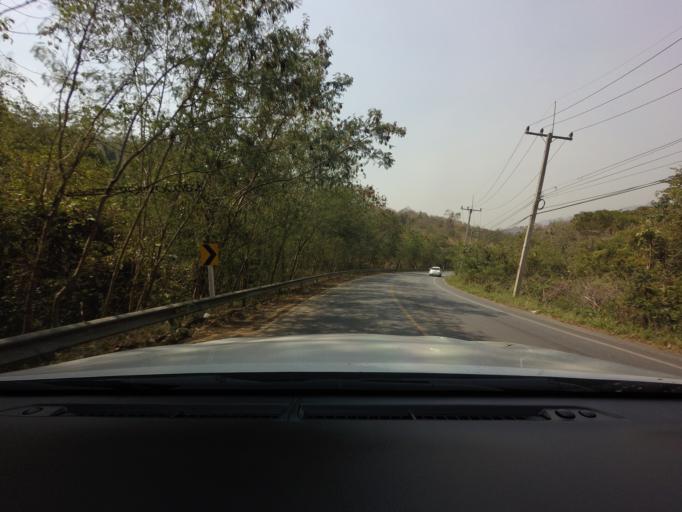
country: TH
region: Sara Buri
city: Muak Lek
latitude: 14.5597
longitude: 101.2995
